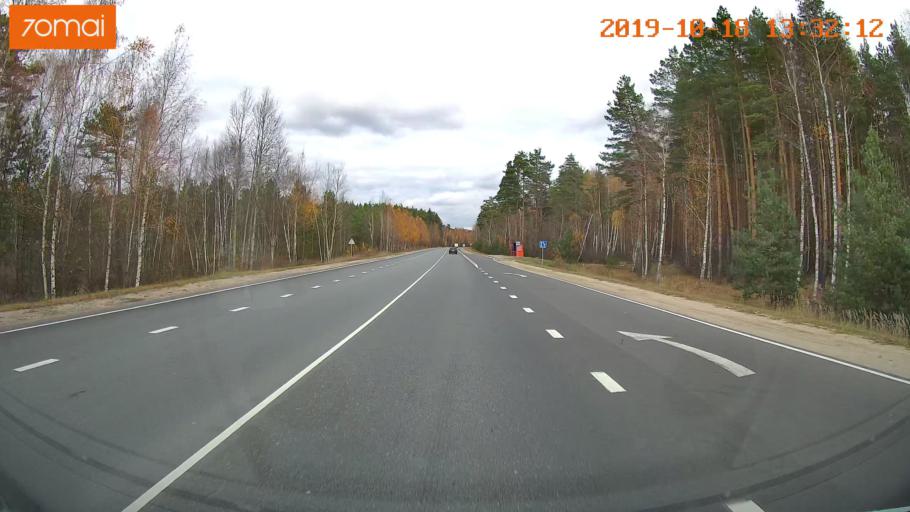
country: RU
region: Rjazan
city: Solotcha
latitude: 54.8299
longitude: 39.9154
